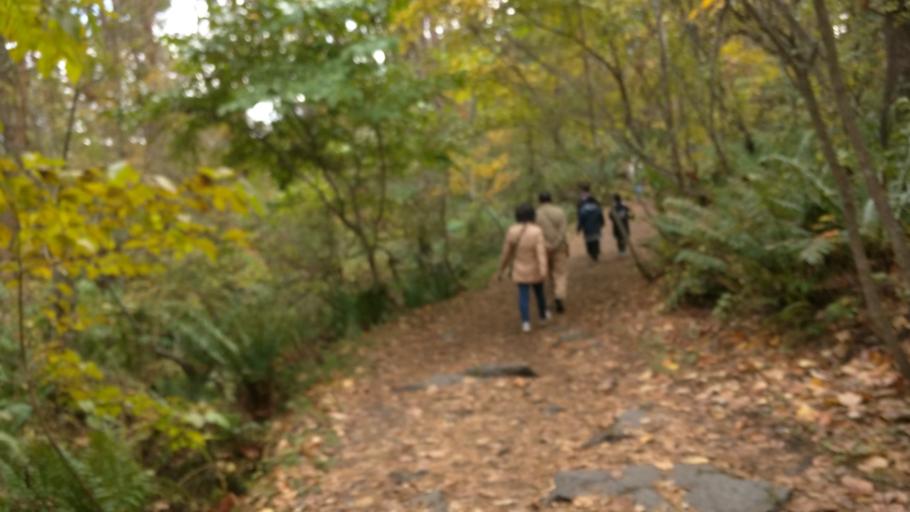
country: JP
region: Fukushima
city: Inawashiro
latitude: 37.6521
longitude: 140.0769
